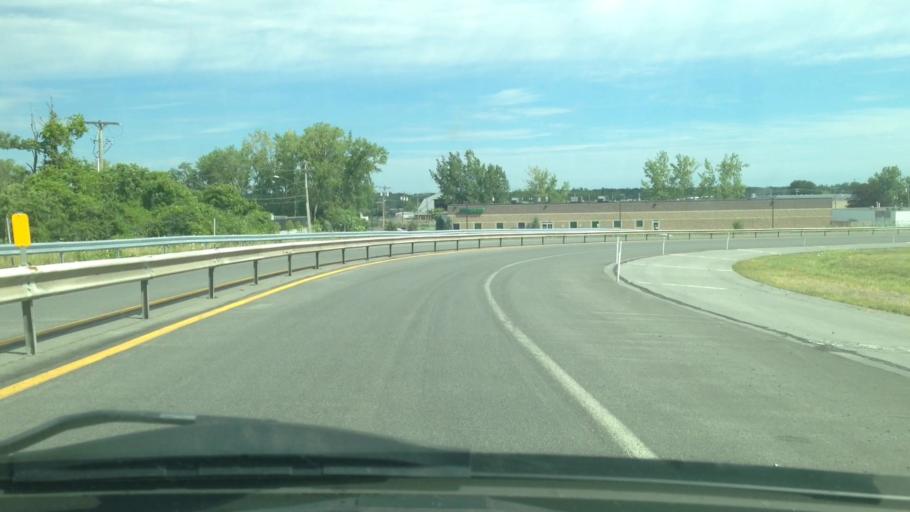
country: US
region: New York
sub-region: Onondaga County
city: East Syracuse
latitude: 43.0937
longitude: -76.0899
